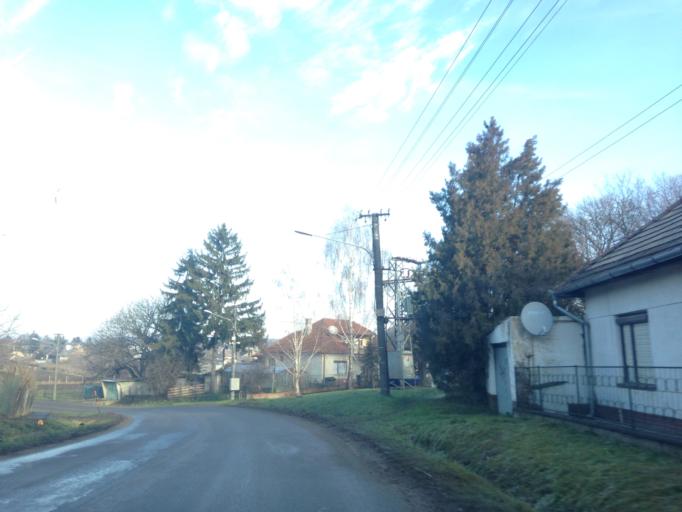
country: SK
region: Nitriansky
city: Svodin
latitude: 47.9526
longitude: 18.4131
